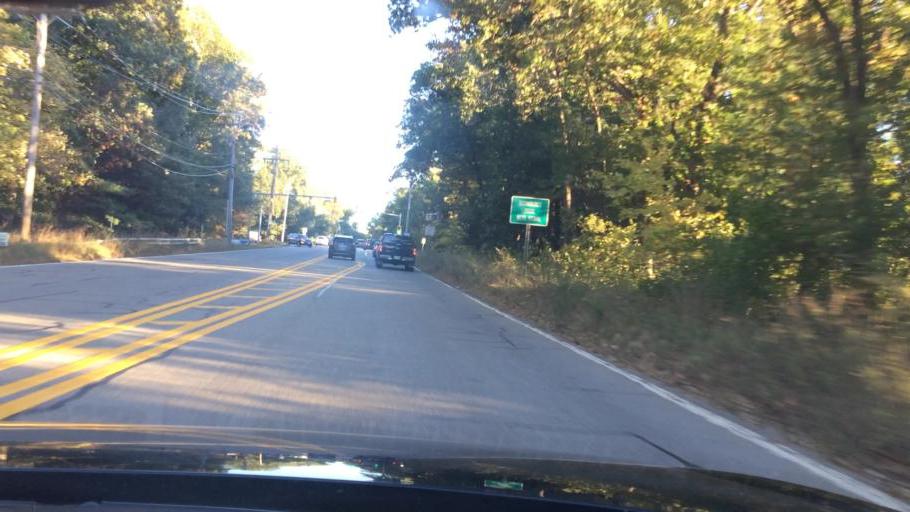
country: US
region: Massachusetts
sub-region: Middlesex County
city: Chelmsford
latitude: 42.6277
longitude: -71.3703
